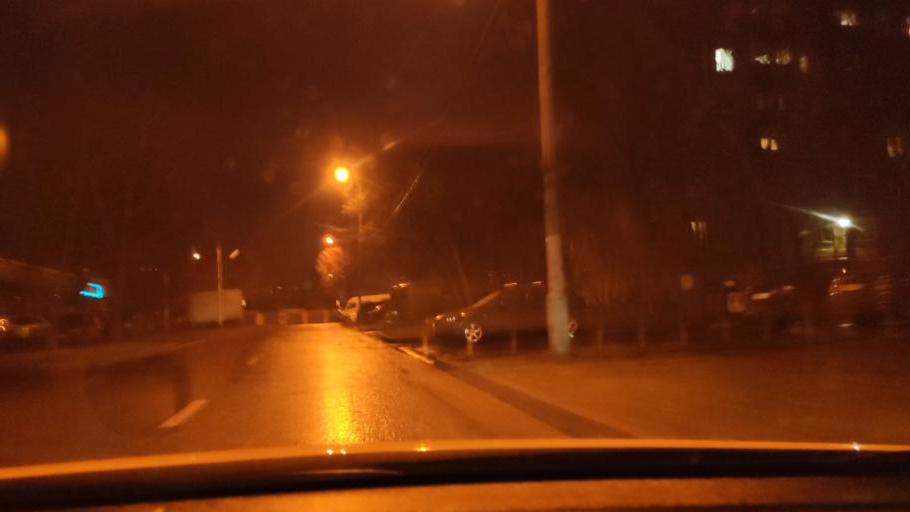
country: RU
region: Moscow
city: Vatutino
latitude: 55.8679
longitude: 37.6884
